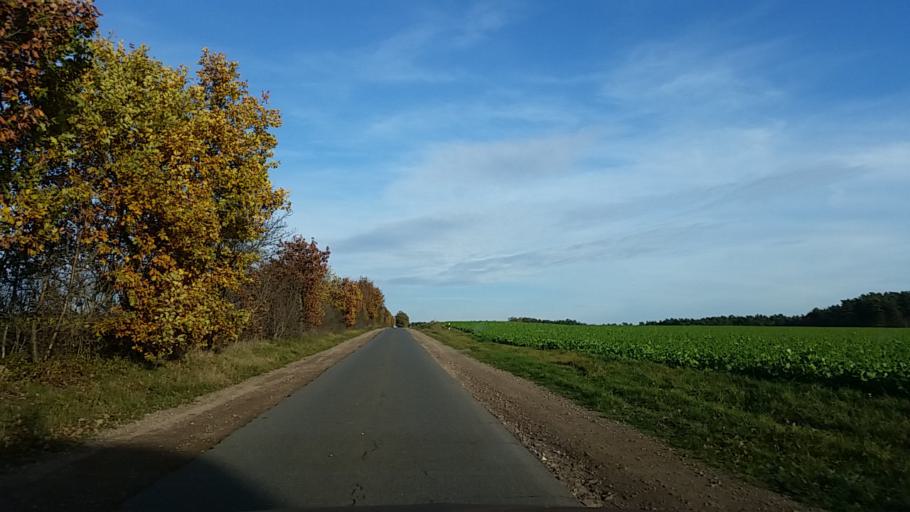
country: DE
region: Lower Saxony
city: Hankensbuttel
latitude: 52.6872
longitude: 10.5787
